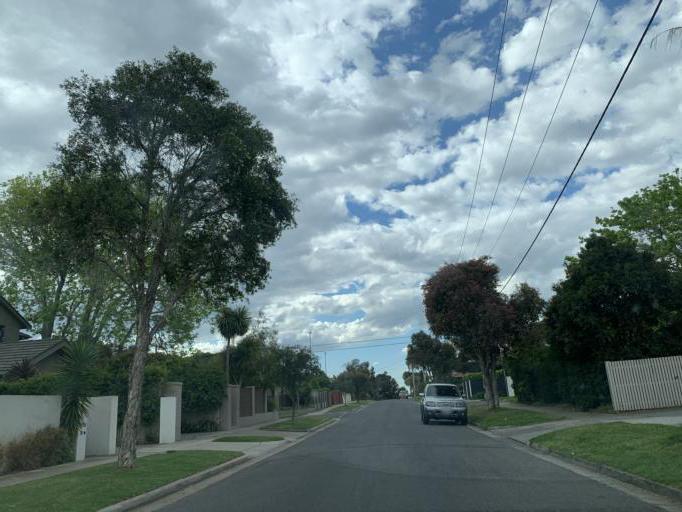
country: AU
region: Victoria
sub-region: Bayside
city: Hampton East
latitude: -37.9366
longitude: 145.0201
